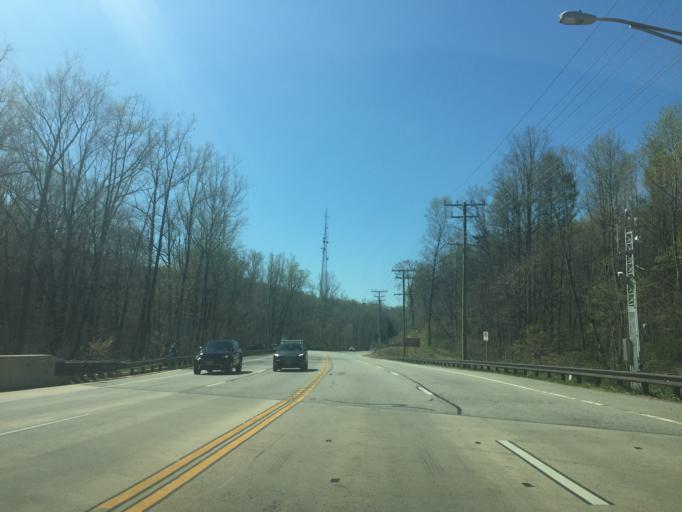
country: US
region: Maryland
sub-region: Harford County
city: Pleasant Hills
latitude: 39.4763
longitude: -76.4085
